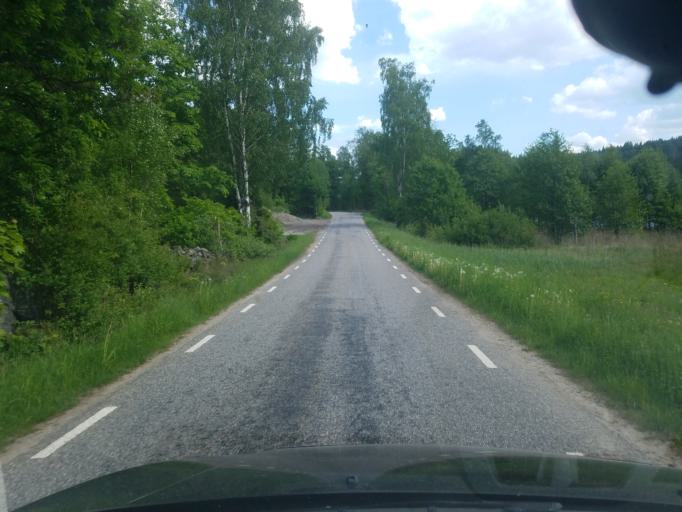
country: SE
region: Vaestra Goetaland
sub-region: Stenungsunds Kommun
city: Stora Hoga
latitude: 57.9986
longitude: 11.9349
